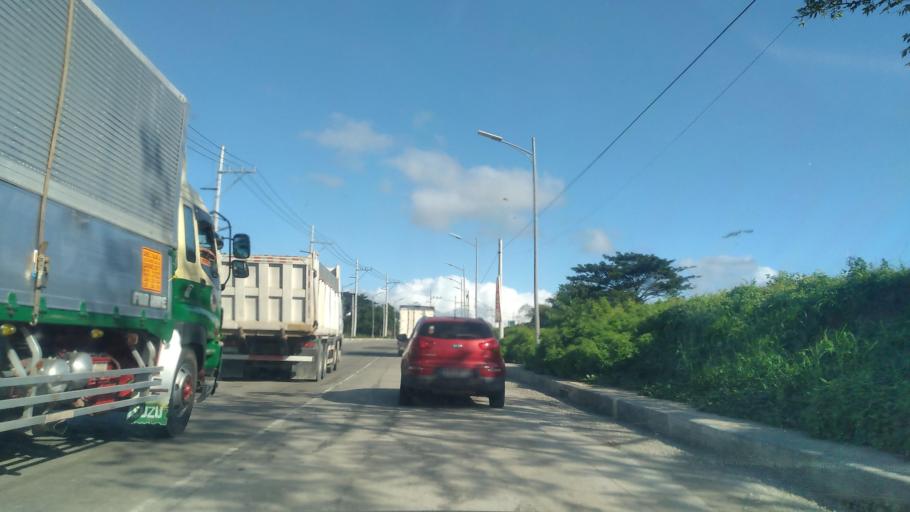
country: PH
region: Calabarzon
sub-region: Province of Quezon
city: Isabang
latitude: 13.9489
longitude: 121.5771
